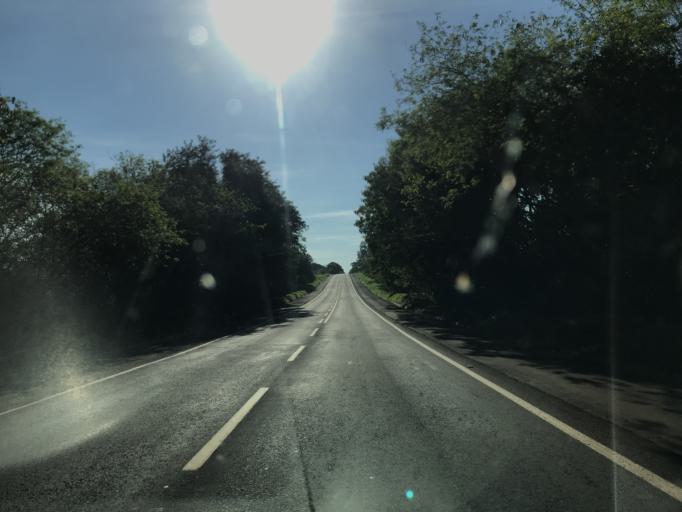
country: BR
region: Parana
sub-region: Ipora
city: Ipora
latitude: -23.9788
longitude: -53.6496
